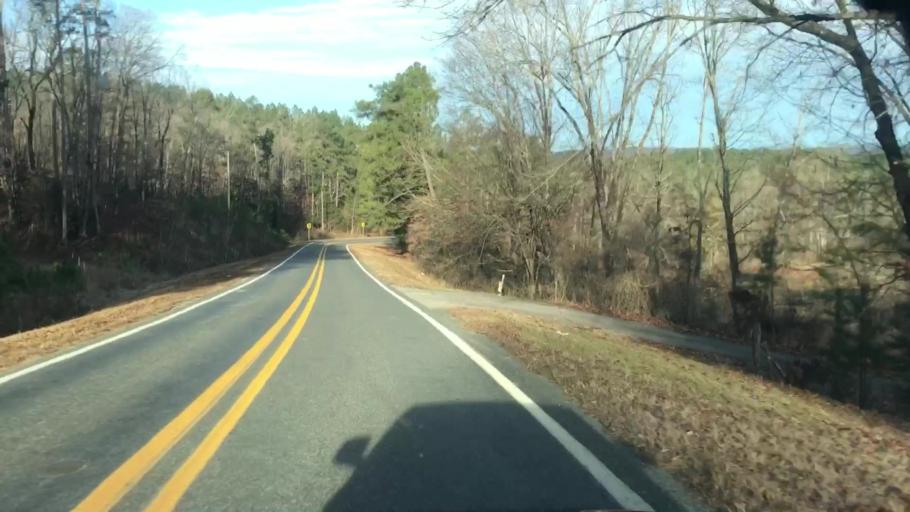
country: US
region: Arkansas
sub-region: Garland County
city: Rockwell
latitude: 34.4880
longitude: -93.2742
